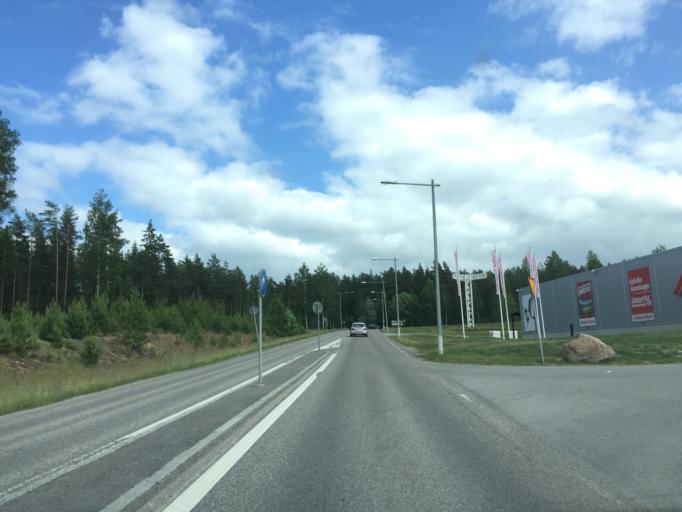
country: SE
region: OErebro
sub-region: Orebro Kommun
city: Orebro
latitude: 59.2204
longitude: 15.1417
